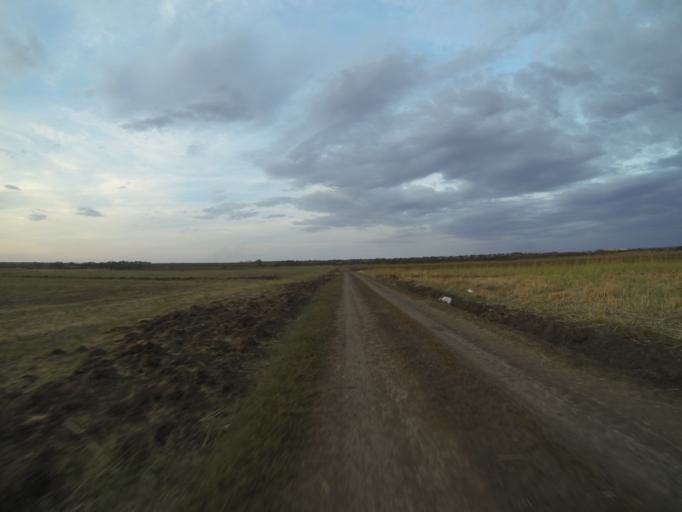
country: RO
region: Dolj
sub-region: Comuna Segarcea
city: Segarcea
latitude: 44.0937
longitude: 23.7207
